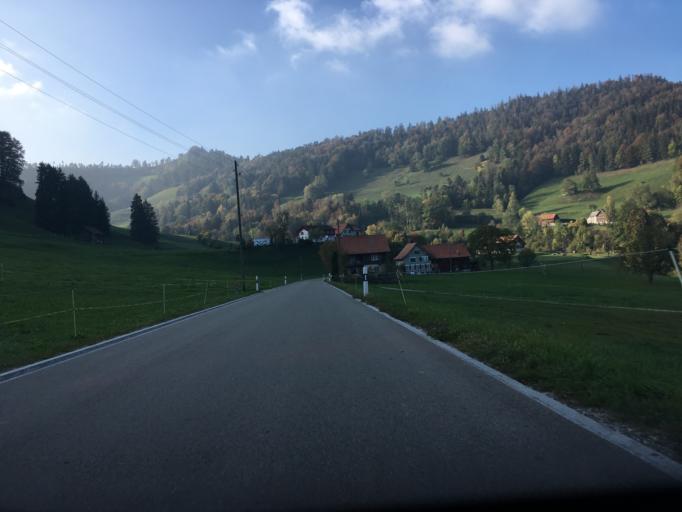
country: CH
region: Saint Gallen
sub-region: Wahlkreis Toggenburg
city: Mosnang
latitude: 47.3435
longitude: 9.0397
